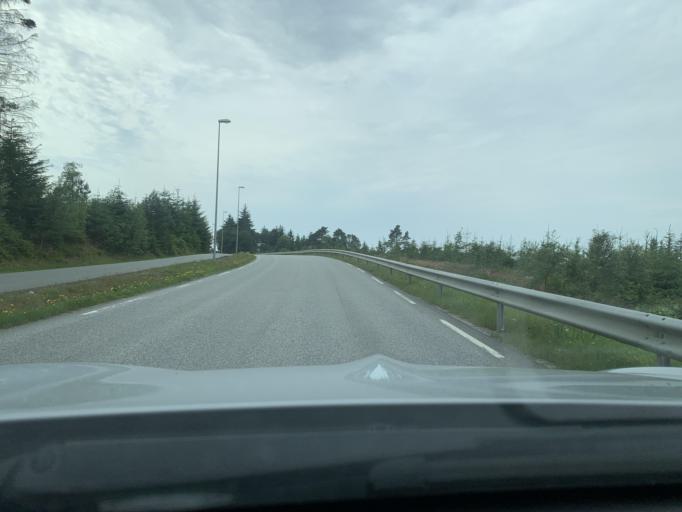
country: NO
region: Rogaland
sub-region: Time
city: Bryne
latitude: 58.7505
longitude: 5.6948
